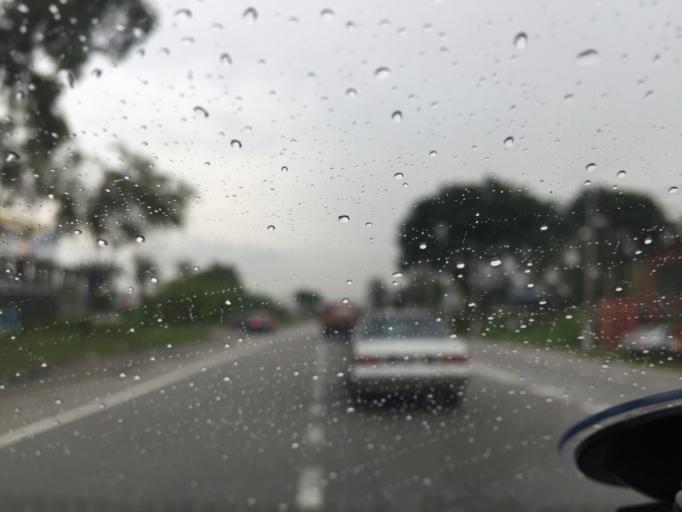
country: MY
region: Selangor
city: Subang Jaya
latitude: 3.0111
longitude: 101.5190
